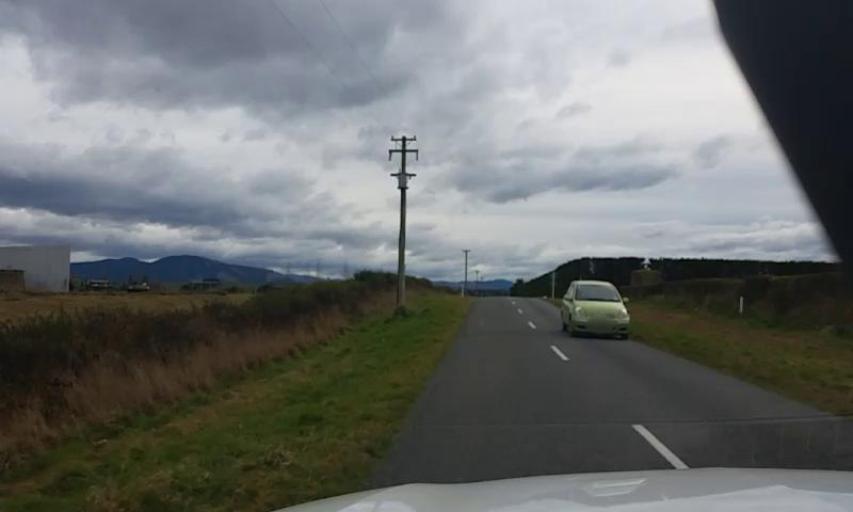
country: NZ
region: Canterbury
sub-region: Waimakariri District
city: Kaiapoi
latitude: -43.2954
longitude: 172.4376
